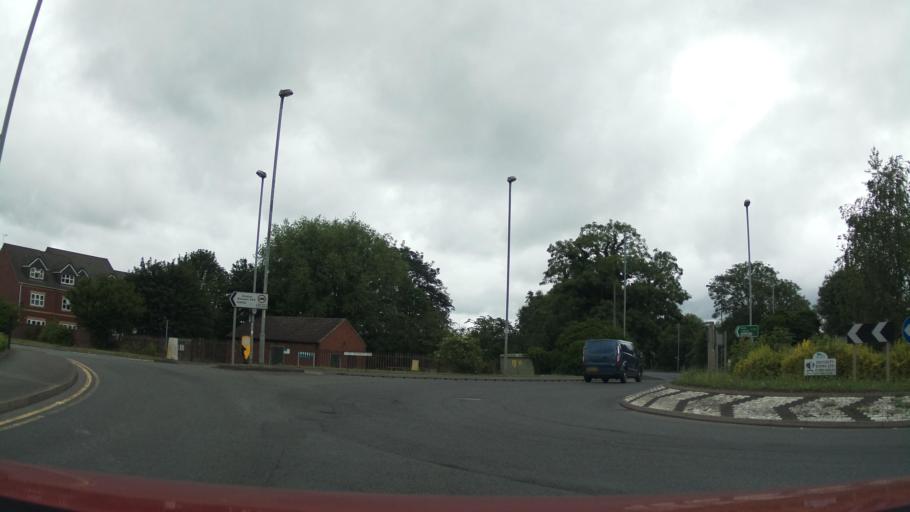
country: GB
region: England
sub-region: Staffordshire
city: Burton upon Trent
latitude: 52.8278
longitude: -1.6175
